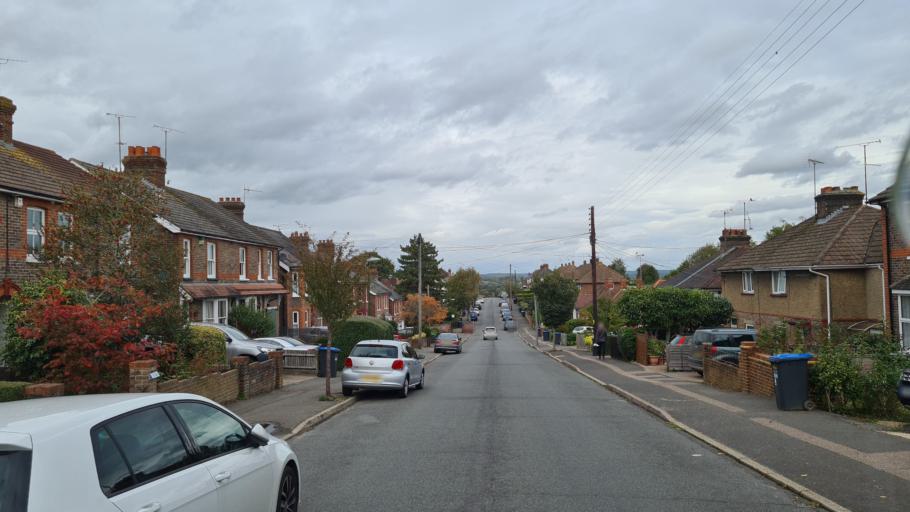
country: GB
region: England
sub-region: West Sussex
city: Haywards Heath
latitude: 50.9953
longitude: -0.0949
